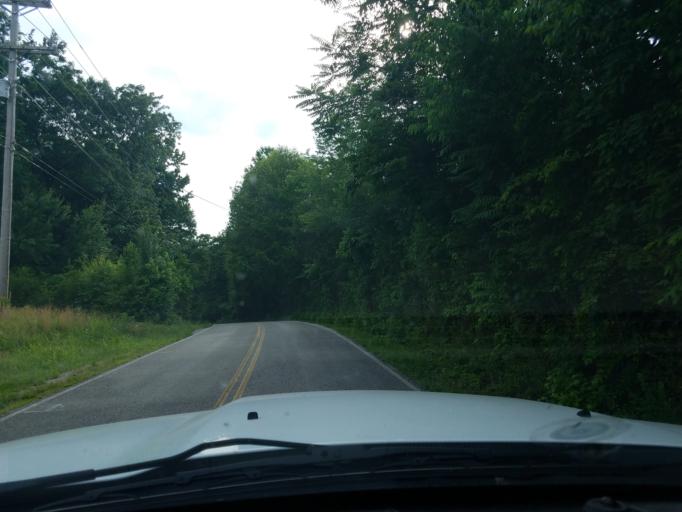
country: US
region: Tennessee
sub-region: Putnam County
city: Cookeville
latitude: 36.1297
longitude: -85.5665
